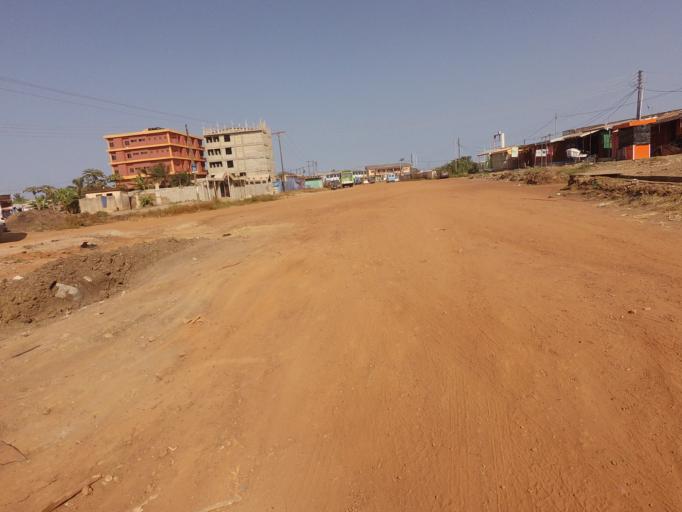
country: GH
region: Greater Accra
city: Teshi Old Town
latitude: 5.5776
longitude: -0.1119
